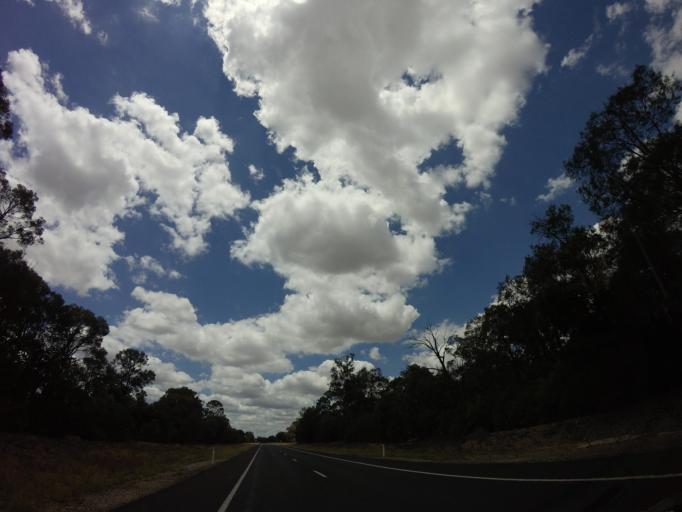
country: AU
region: Queensland
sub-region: Goondiwindi
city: Goondiwindi
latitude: -28.1116
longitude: 150.7173
